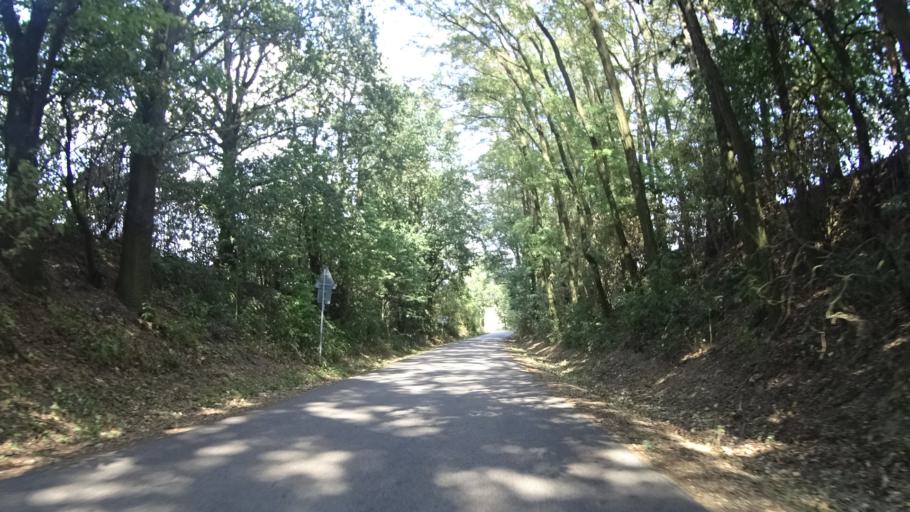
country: CZ
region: Kralovehradecky
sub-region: Okres Jicin
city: Sobotka
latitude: 50.4449
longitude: 15.2303
